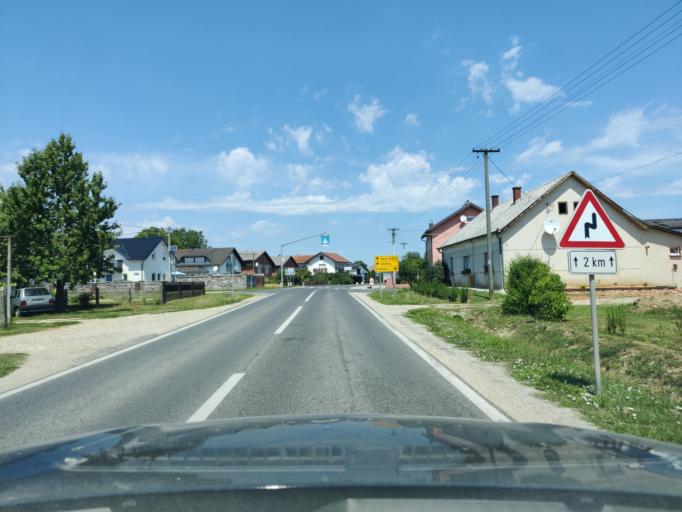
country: HR
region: Medimurska
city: Mackovec
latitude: 46.4402
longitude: 16.4308
